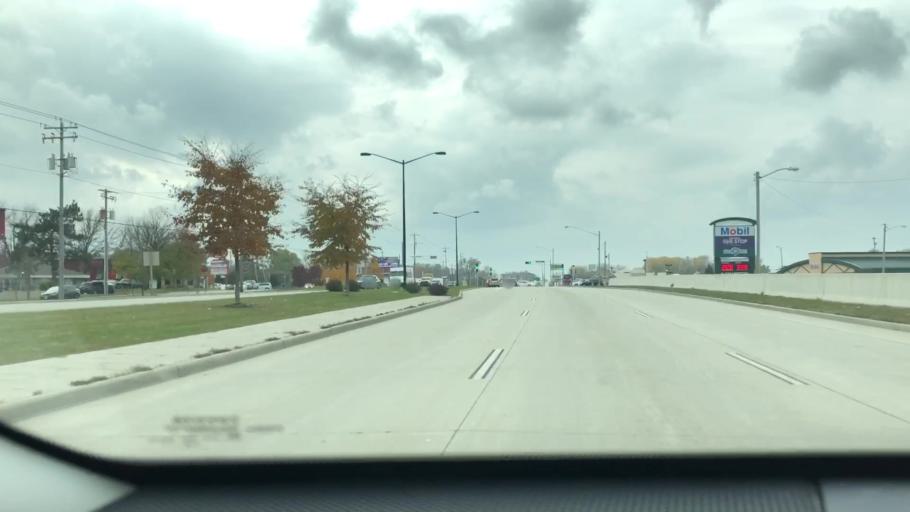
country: US
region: Wisconsin
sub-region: Brown County
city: Howard
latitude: 44.5242
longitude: -88.0870
